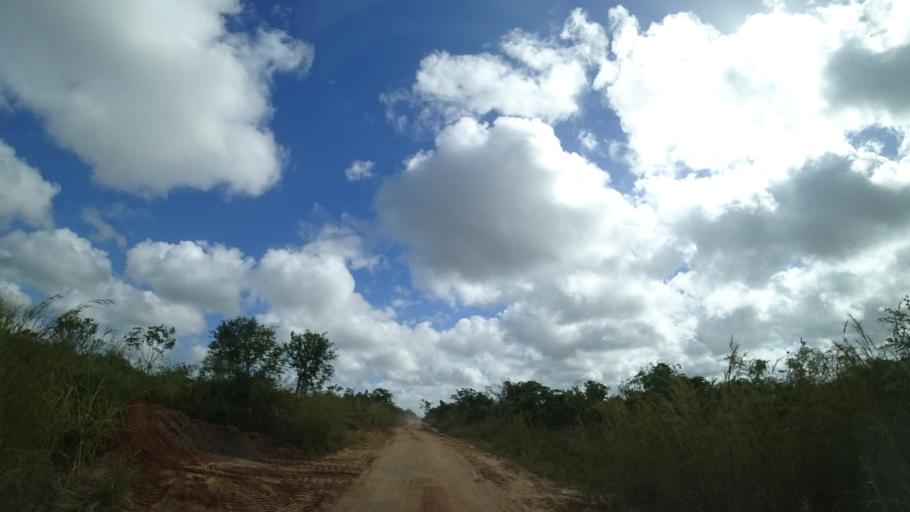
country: MZ
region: Sofala
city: Dondo
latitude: -19.4448
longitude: 34.7164
